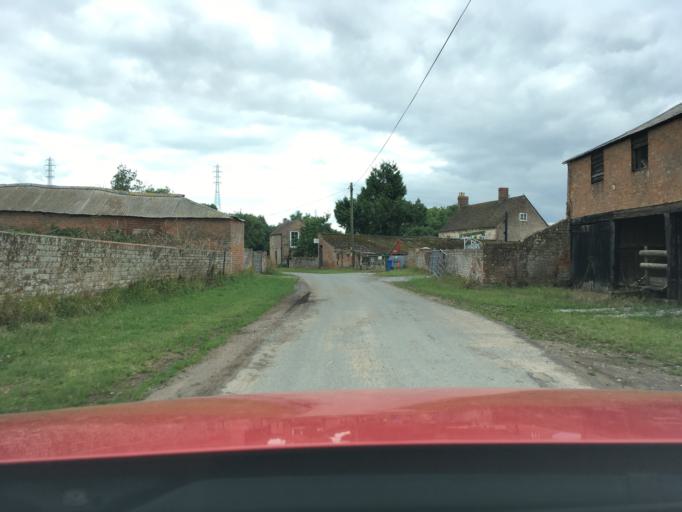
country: GB
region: England
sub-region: Gloucestershire
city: Cinderford
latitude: 51.7920
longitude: -2.4269
